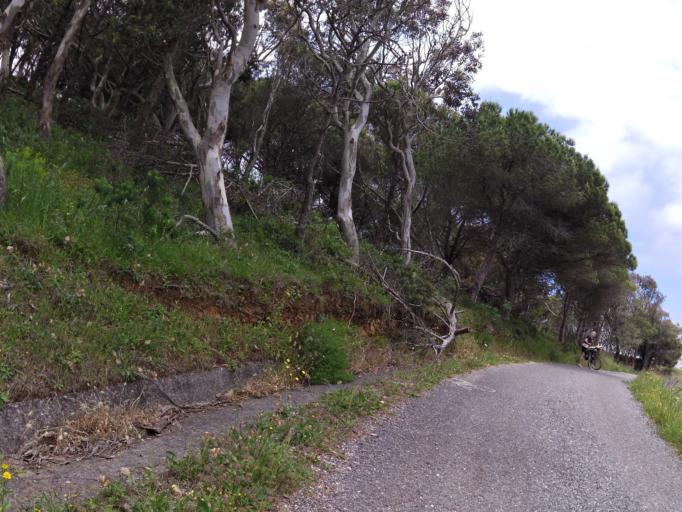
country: PT
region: Faro
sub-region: Vila do Bispo
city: Vila do Bispo
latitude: 37.0781
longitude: -8.8780
